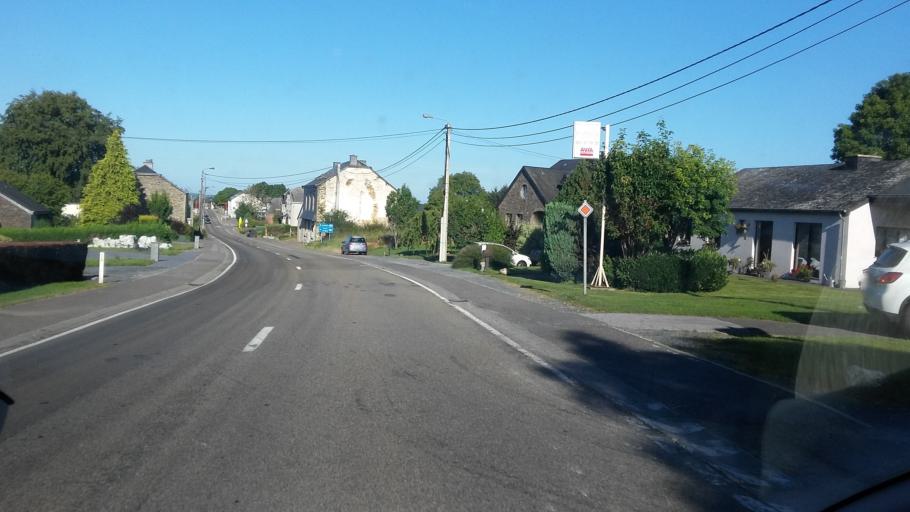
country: BE
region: Wallonia
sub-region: Province du Luxembourg
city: Neufchateau
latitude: 49.8369
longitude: 5.4611
